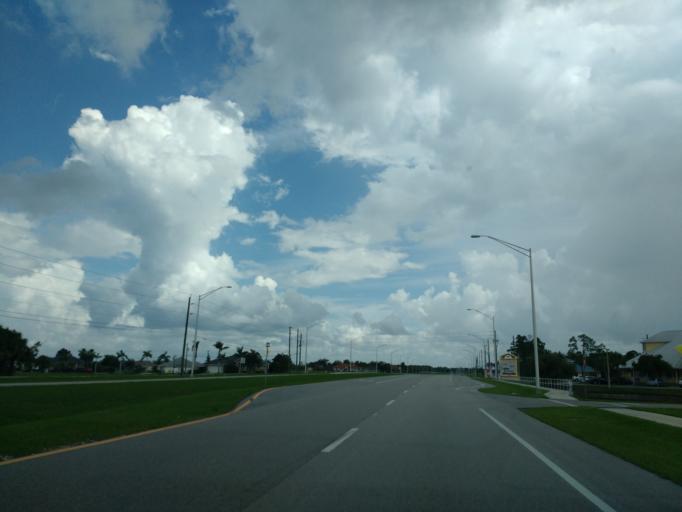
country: US
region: Florida
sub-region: Lee County
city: Burnt Store Marina
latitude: 26.7853
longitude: -82.0379
